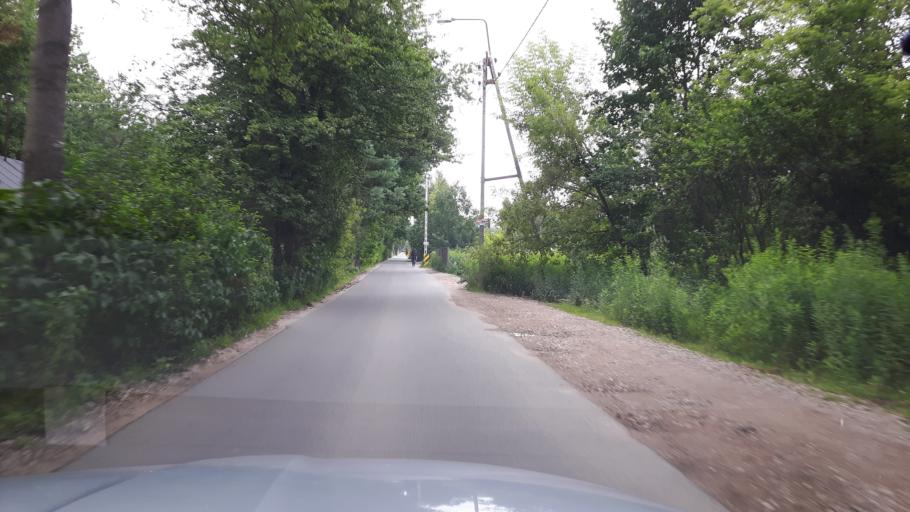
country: PL
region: Masovian Voivodeship
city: Zielonka
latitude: 52.2895
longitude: 21.1666
